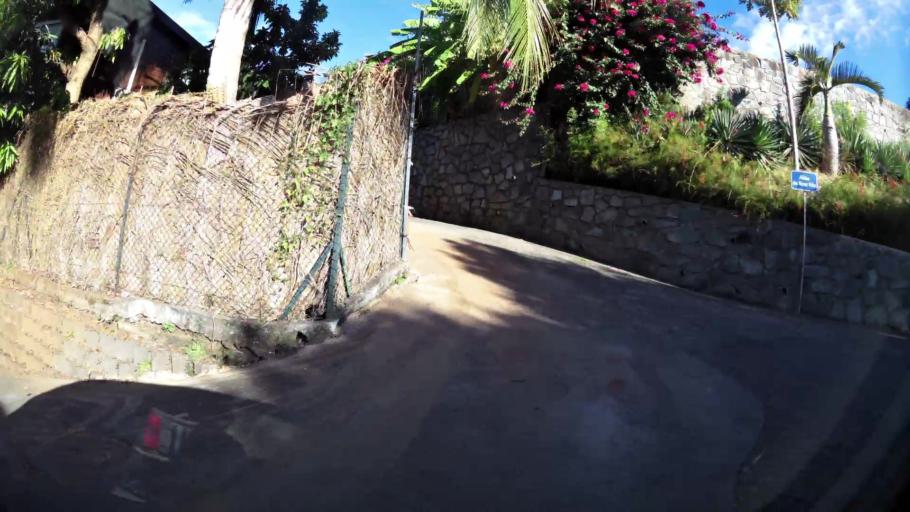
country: YT
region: Koungou
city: Koungou
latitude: -12.7438
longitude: 45.2158
